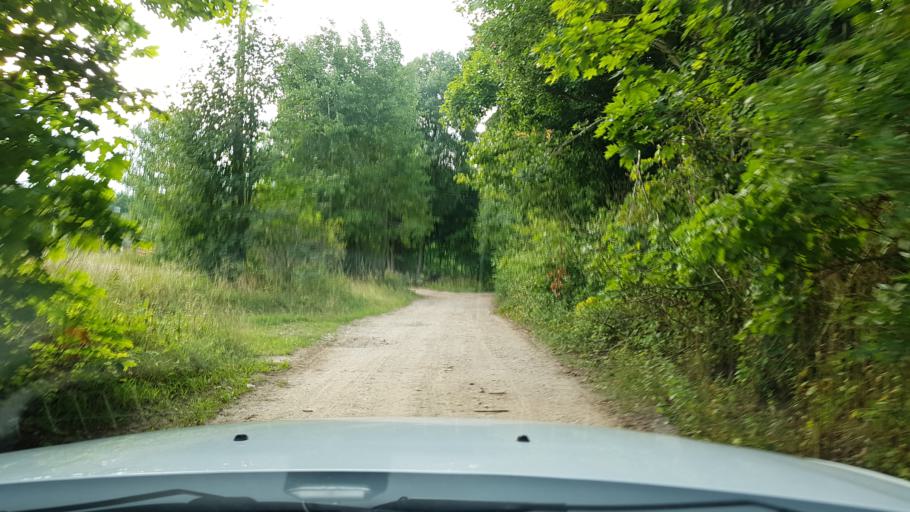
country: PL
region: West Pomeranian Voivodeship
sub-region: Powiat swidwinski
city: Polczyn-Zdroj
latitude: 53.8009
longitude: 16.0759
